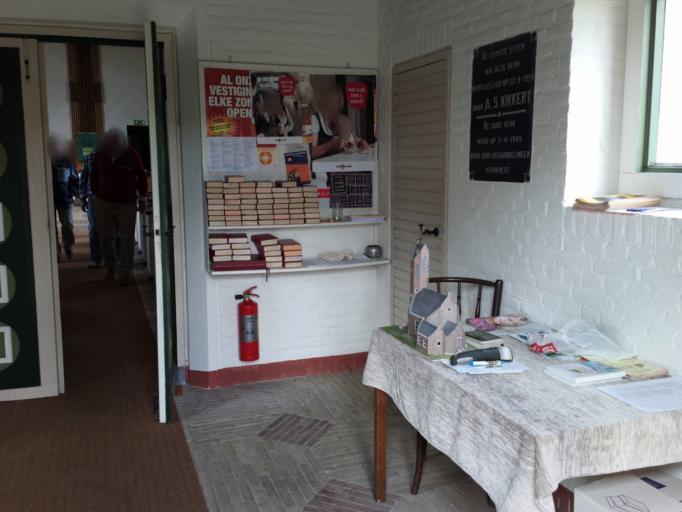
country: NL
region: North Holland
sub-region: Gemeente Texel
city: Den Burg
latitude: 53.0727
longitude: 4.8208
